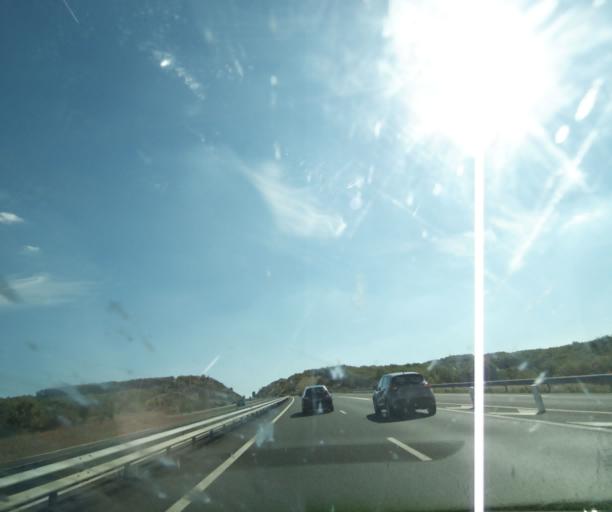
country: FR
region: Limousin
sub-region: Departement de la Correze
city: Brive-la-Gaillarde
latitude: 45.0621
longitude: 1.5062
